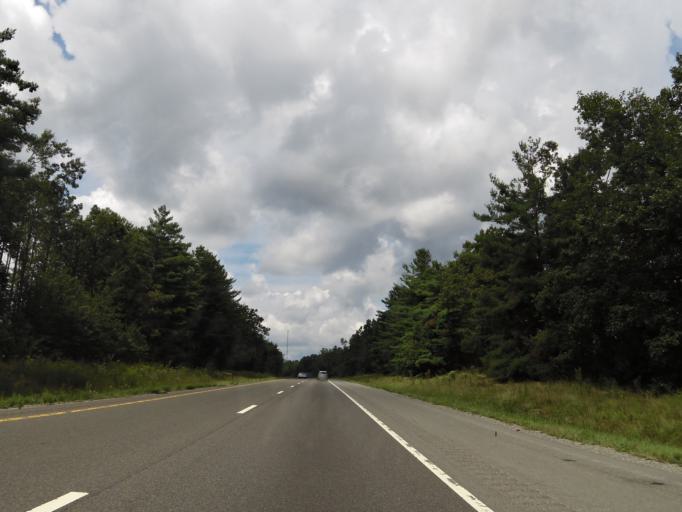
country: US
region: Tennessee
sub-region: Cumberland County
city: Crossville
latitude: 36.0431
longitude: -85.1158
